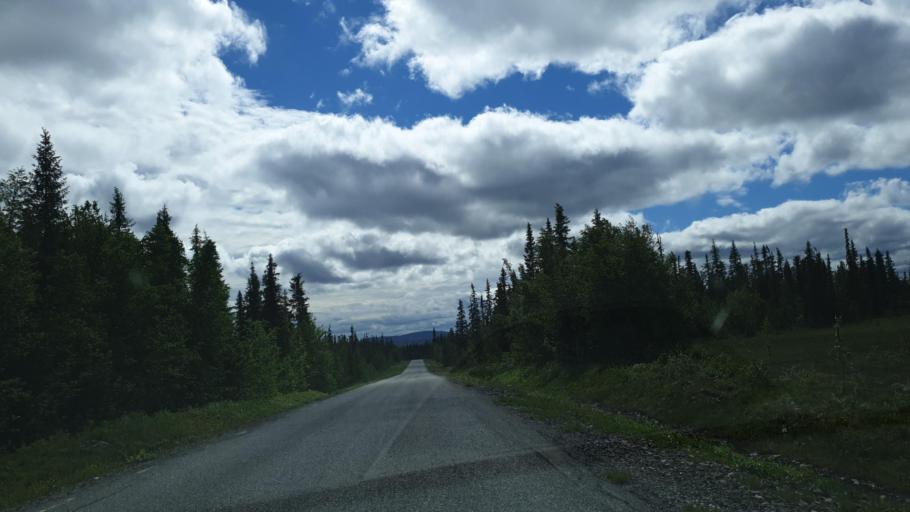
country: SE
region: Vaesterbotten
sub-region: Vilhelmina Kommun
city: Sjoberg
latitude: 65.0944
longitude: 15.8704
